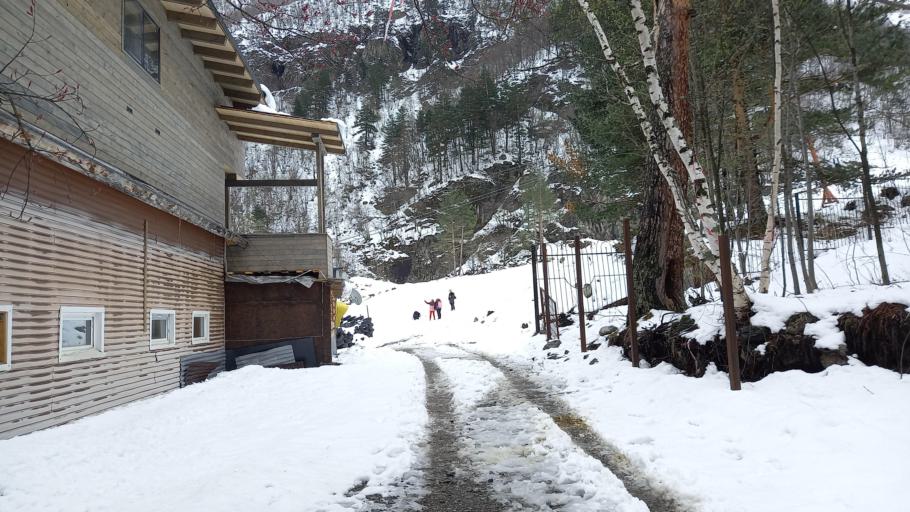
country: RU
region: North Ossetia
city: Mizur
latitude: 42.7851
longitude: 43.9047
